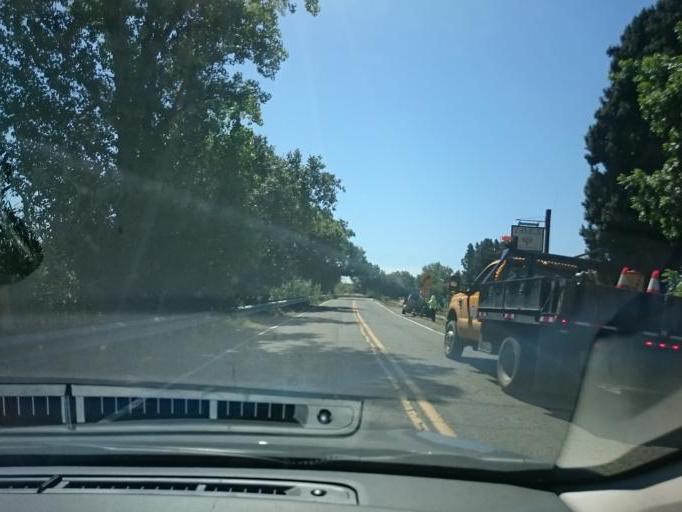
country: US
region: California
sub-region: Sacramento County
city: Parkway
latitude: 38.4708
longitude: -121.5078
